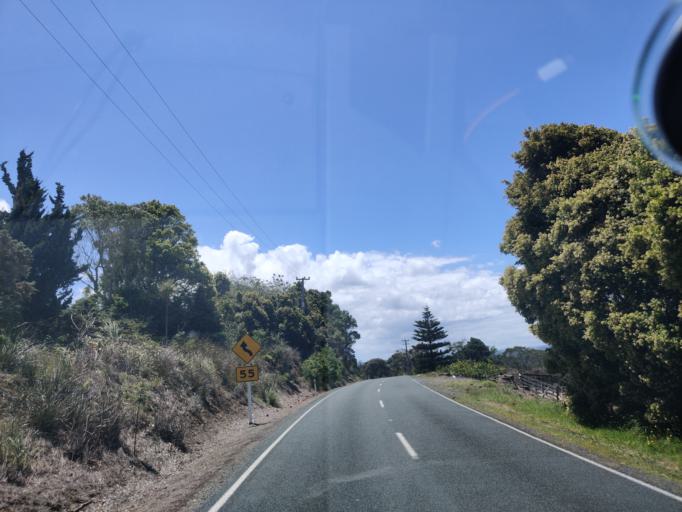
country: NZ
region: Northland
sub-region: Far North District
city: Kaitaia
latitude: -35.0240
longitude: 173.2110
